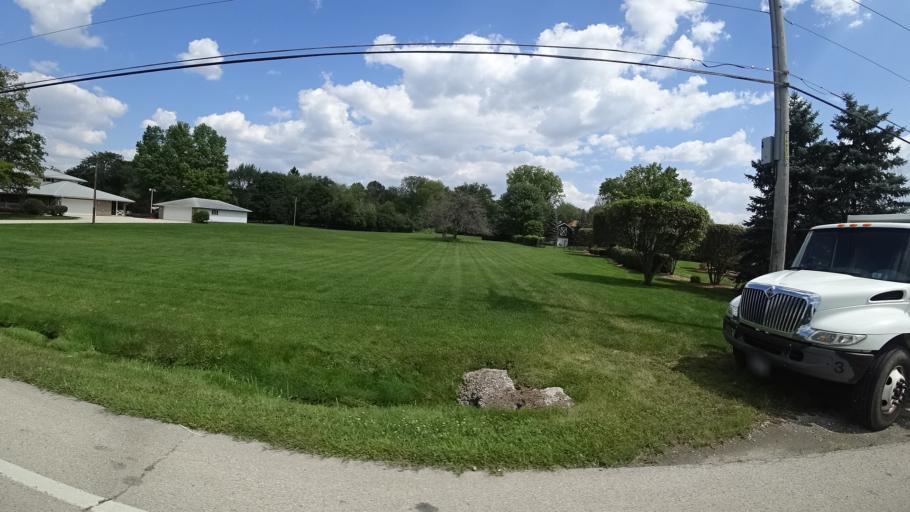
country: US
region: Illinois
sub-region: Cook County
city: Orland Park
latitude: 41.6207
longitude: -87.8193
